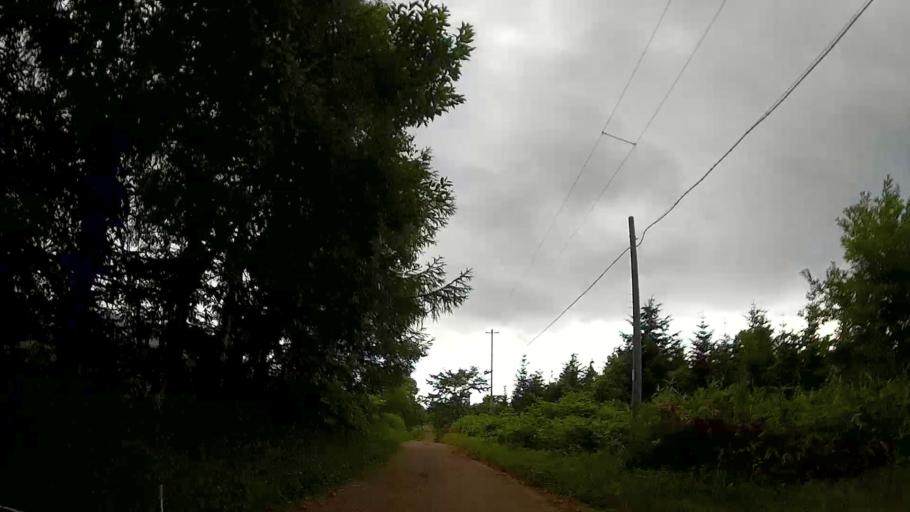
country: JP
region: Hokkaido
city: Nanae
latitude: 42.1268
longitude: 140.4105
